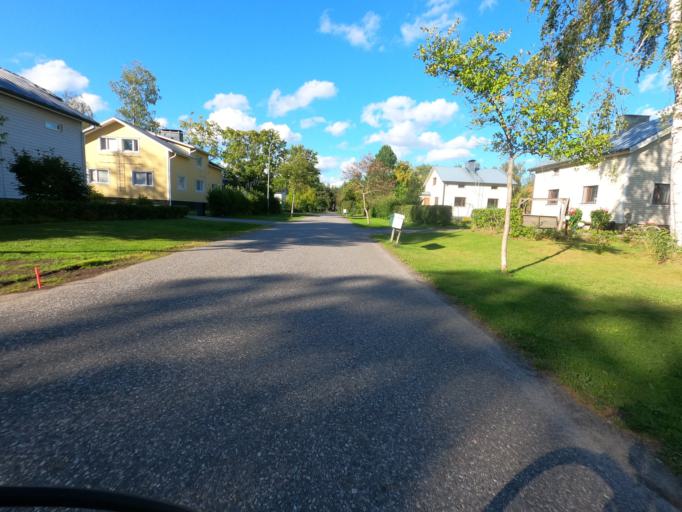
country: FI
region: North Karelia
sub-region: Joensuu
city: Joensuu
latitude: 62.6088
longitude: 29.7501
